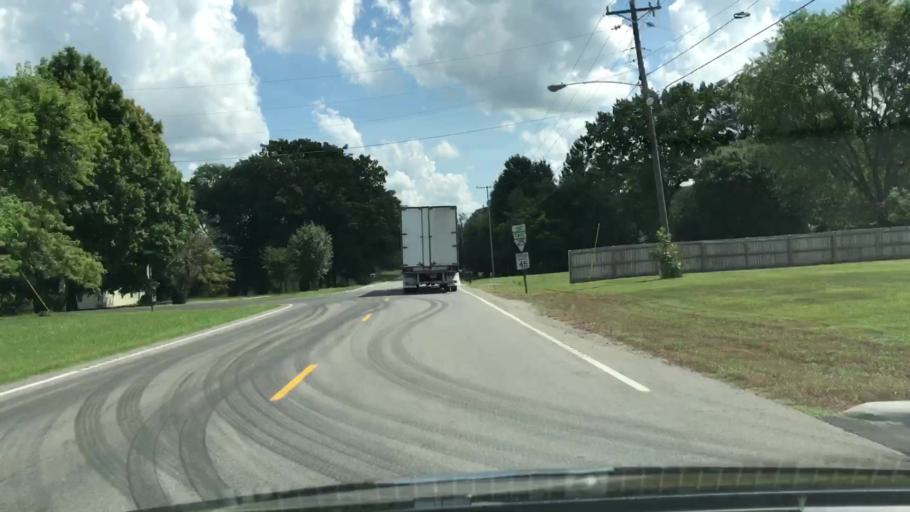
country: US
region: Tennessee
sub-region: Robertson County
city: Cross Plains
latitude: 36.5369
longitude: -86.6588
